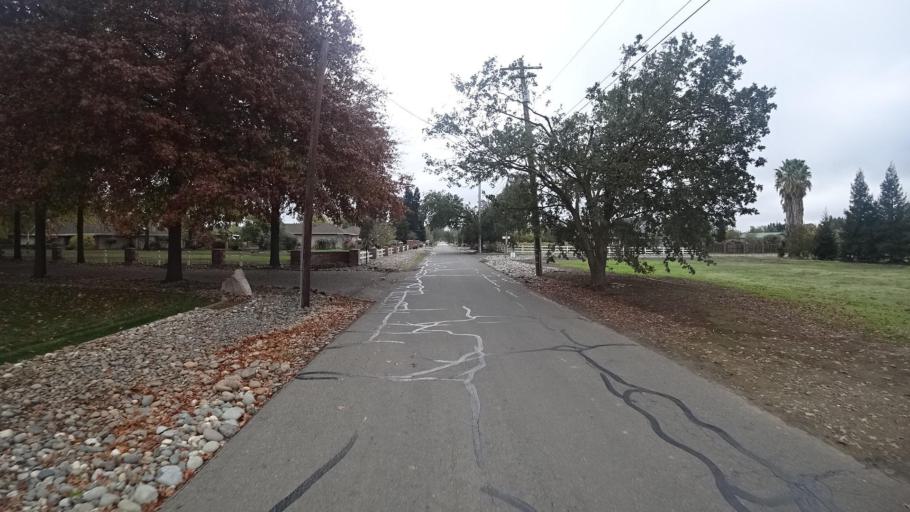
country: US
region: California
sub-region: Sacramento County
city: Wilton
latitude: 38.4428
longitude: -121.3024
